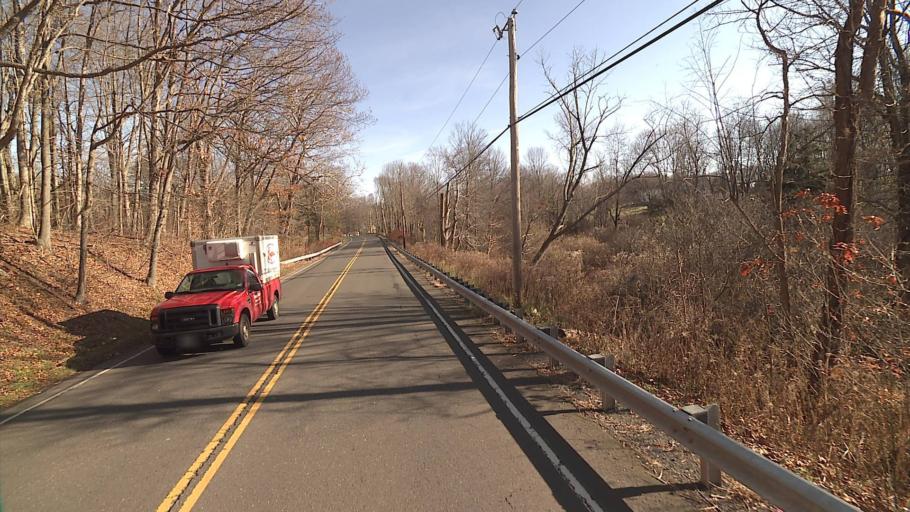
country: US
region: Connecticut
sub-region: Middlesex County
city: Durham
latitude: 41.4369
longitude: -72.7215
